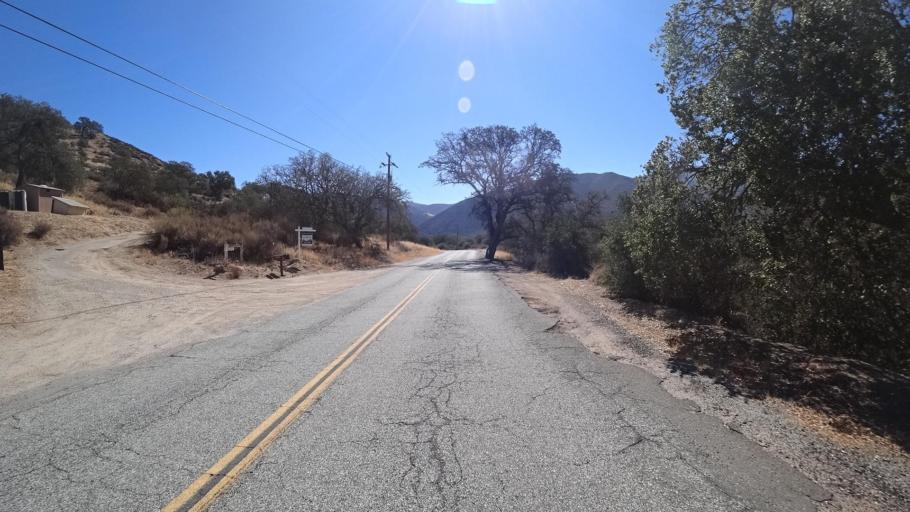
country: US
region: California
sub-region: Monterey County
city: Greenfield
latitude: 36.2589
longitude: -121.4280
